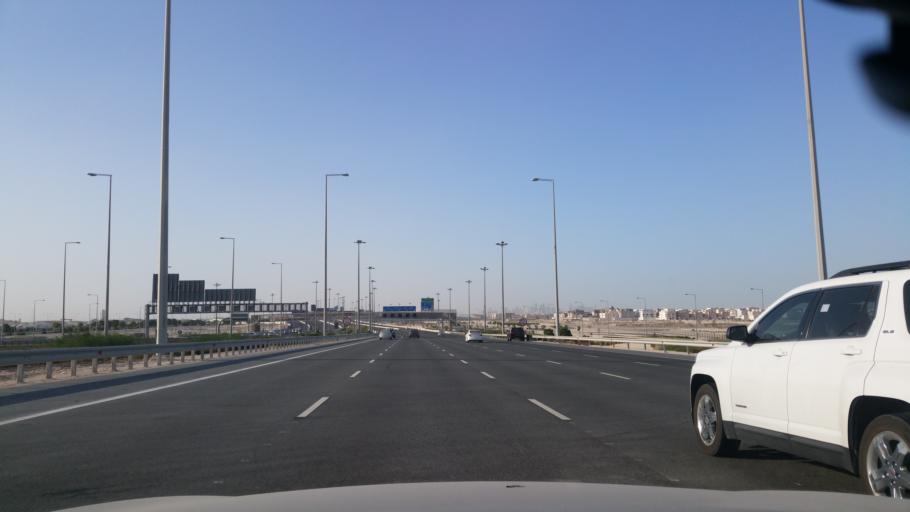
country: QA
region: Al Wakrah
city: Al Wukayr
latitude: 25.2087
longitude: 51.5399
